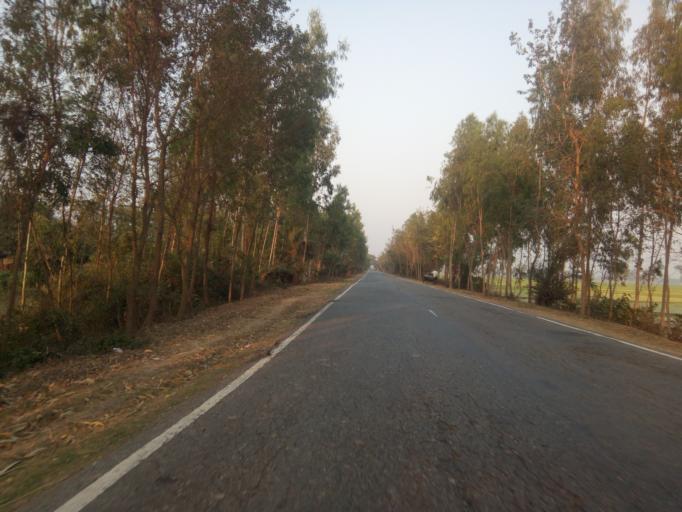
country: BD
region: Rajshahi
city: Bogra
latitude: 24.5746
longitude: 89.2185
